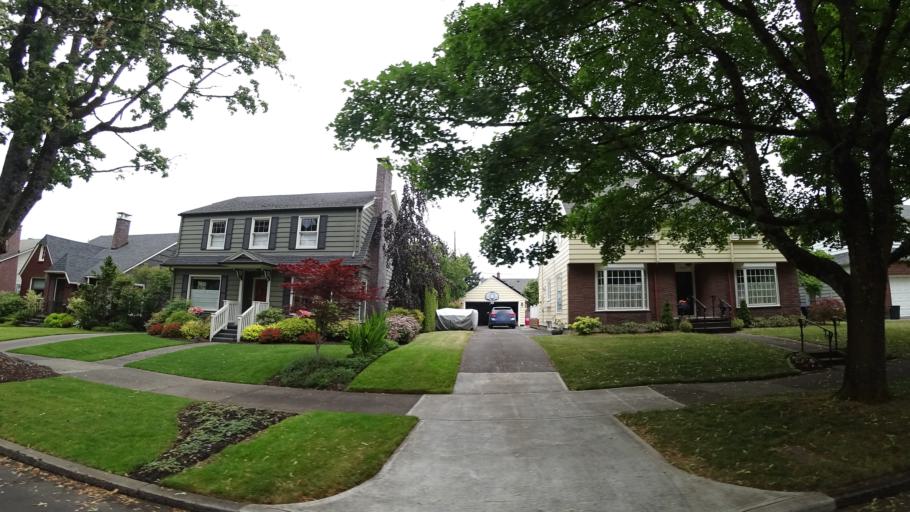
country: US
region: Oregon
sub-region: Multnomah County
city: Portland
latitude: 45.5745
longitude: -122.7039
